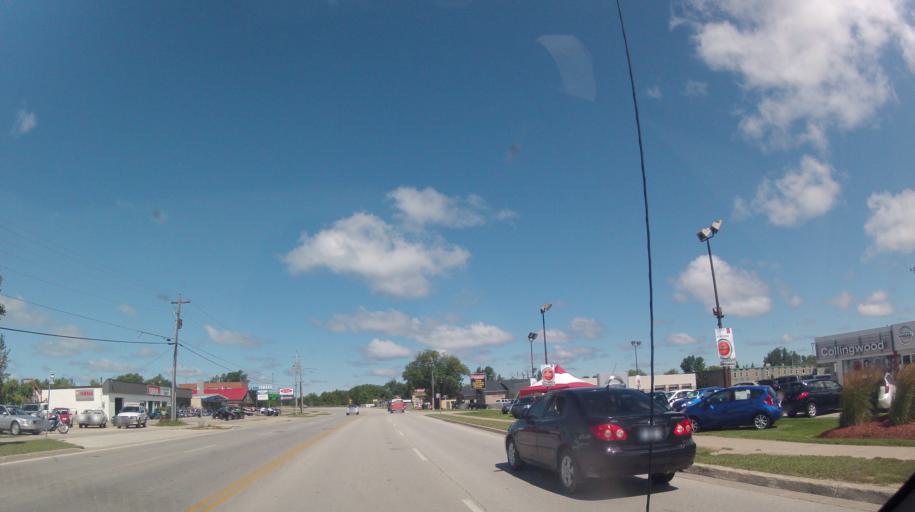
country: CA
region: Ontario
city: Collingwood
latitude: 44.5004
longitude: -80.1963
